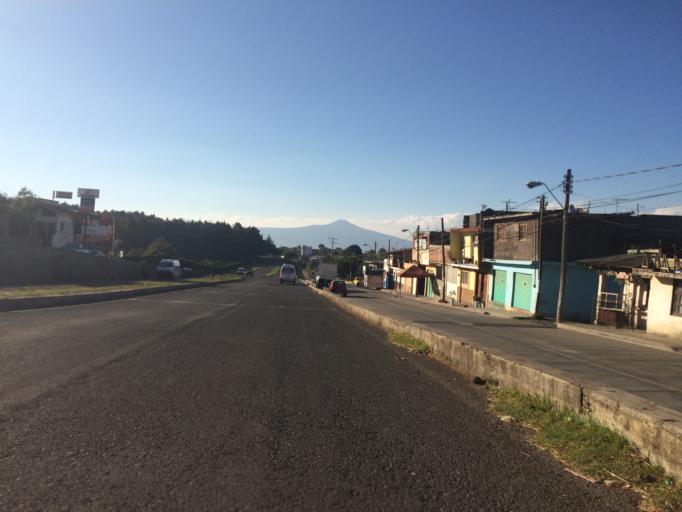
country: MX
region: Michoacan
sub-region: Patzcuaro
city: Colonia Vista Bella (Lomas del Peaje)
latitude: 19.5020
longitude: -101.6027
